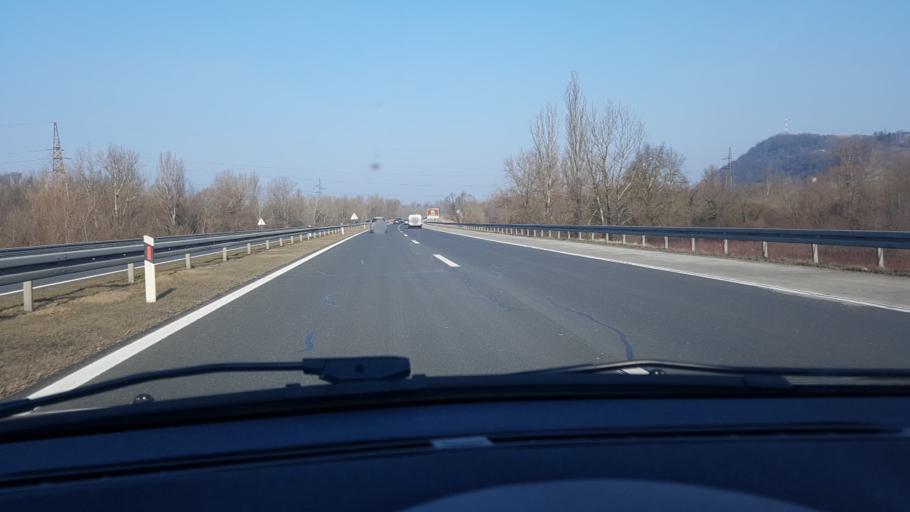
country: HR
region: Zagrebacka
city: Bestovje
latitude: 45.8136
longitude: 15.8271
